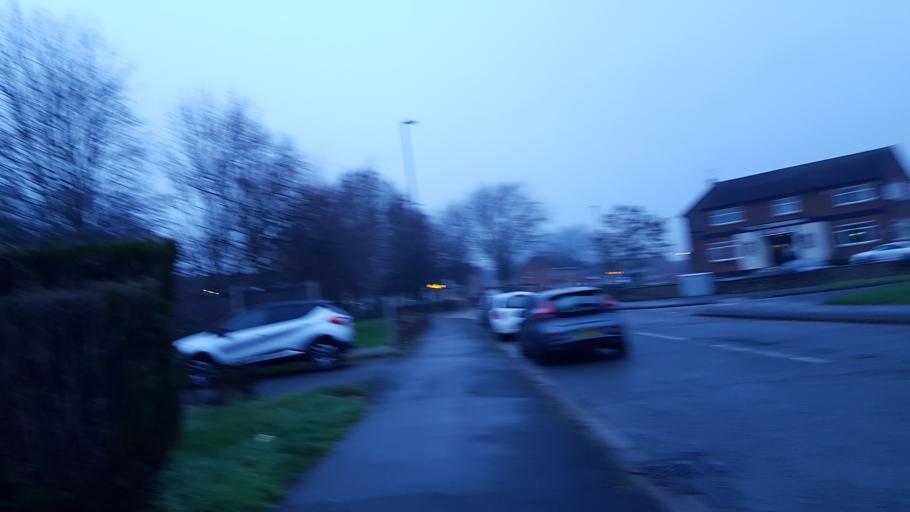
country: GB
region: England
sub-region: Derbyshire
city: Borrowash
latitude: 52.8875
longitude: -1.4216
